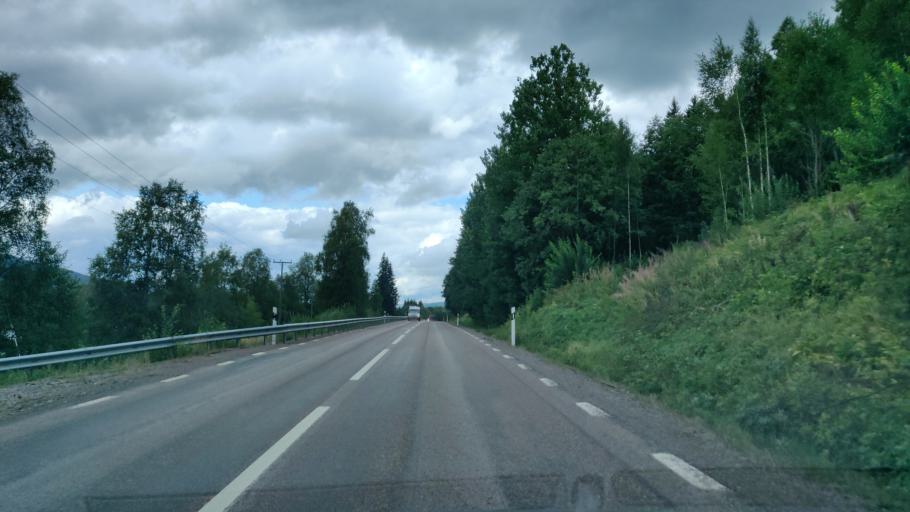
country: SE
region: Vaermland
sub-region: Torsby Kommun
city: Torsby
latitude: 60.5778
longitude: 13.0849
